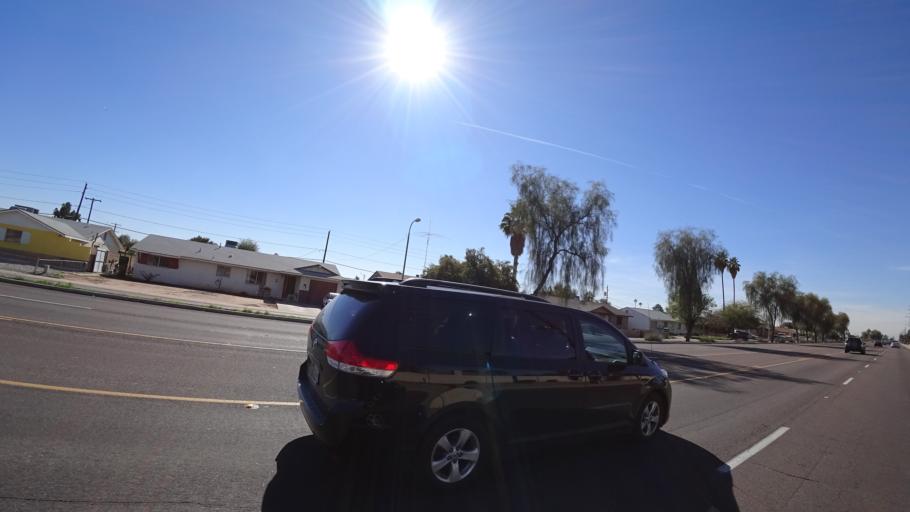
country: US
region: Arizona
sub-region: Maricopa County
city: Glendale
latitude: 33.5093
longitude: -112.2085
